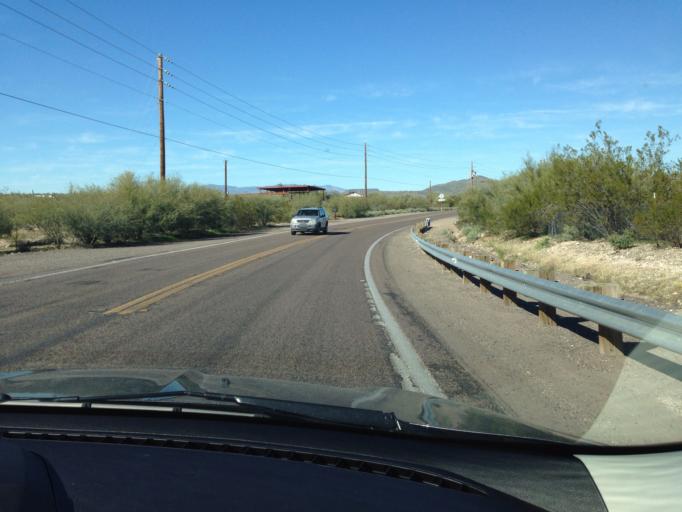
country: US
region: Arizona
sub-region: Maricopa County
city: New River
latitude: 33.8938
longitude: -112.0768
